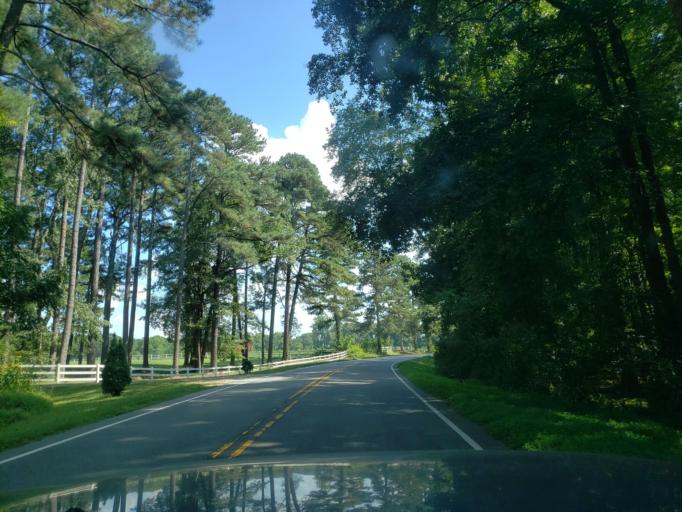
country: US
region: North Carolina
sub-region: Wake County
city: West Raleigh
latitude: 35.9222
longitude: -78.6857
